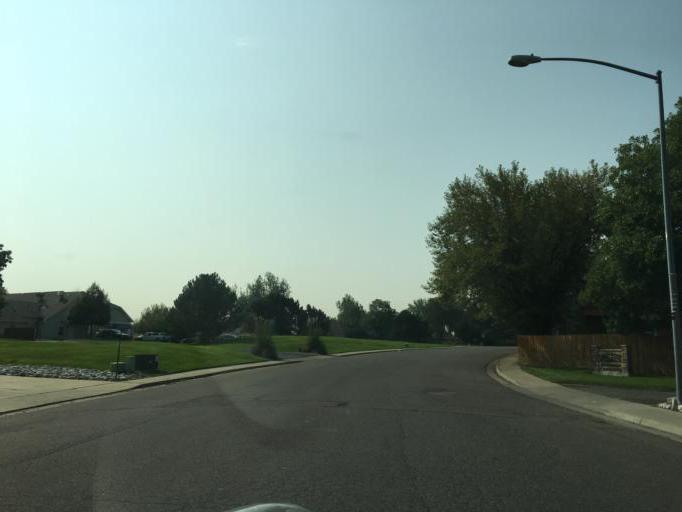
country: US
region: Colorado
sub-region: Adams County
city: Brighton
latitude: 39.9849
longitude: -104.7943
